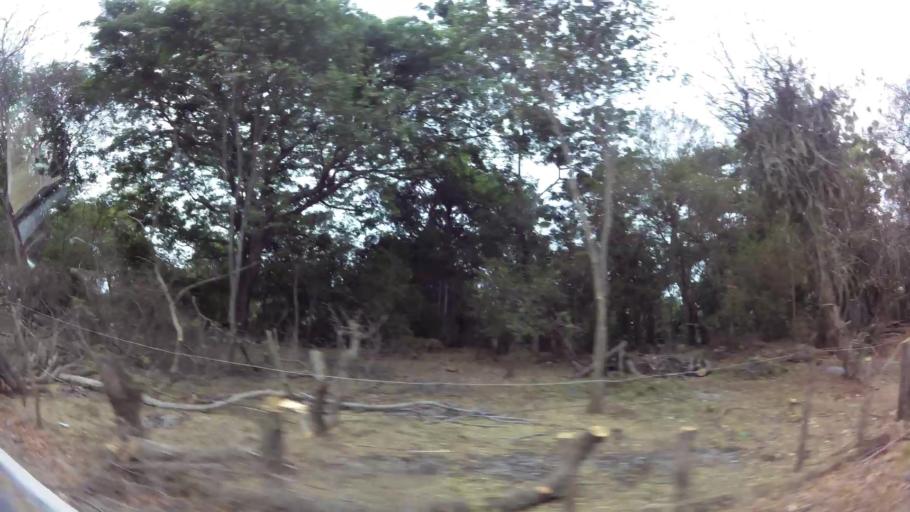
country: NI
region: Masaya
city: Ticuantepe
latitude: 12.0884
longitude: -86.1858
